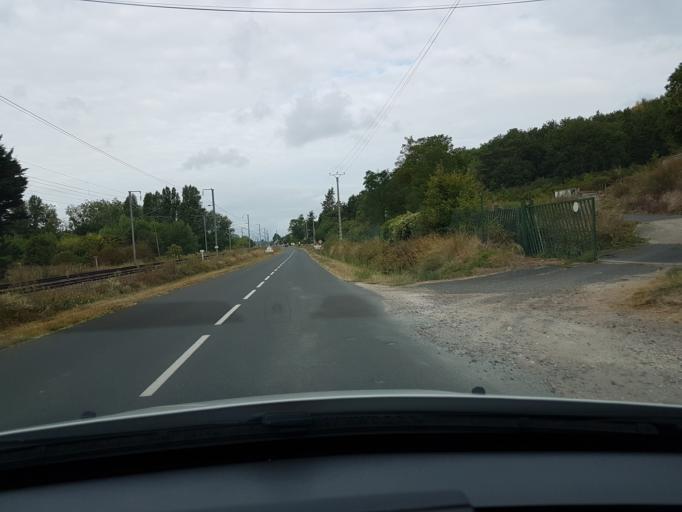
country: FR
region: Centre
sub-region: Departement d'Indre-et-Loire
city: Saint-Martin-le-Beau
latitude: 47.3493
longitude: 0.9364
